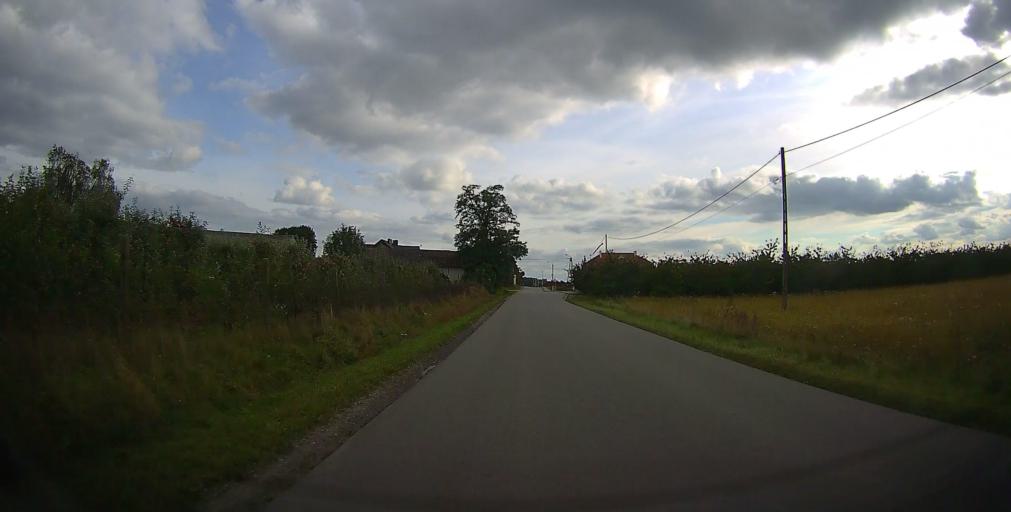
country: PL
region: Masovian Voivodeship
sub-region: Powiat bialobrzeski
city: Promna
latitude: 51.7131
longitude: 20.9582
